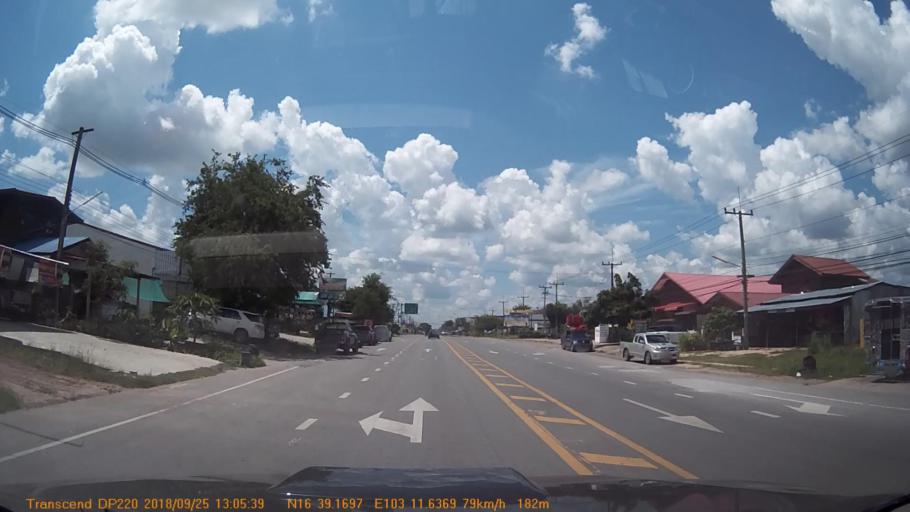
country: TH
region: Kalasin
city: Huai Mek
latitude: 16.6528
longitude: 103.1941
